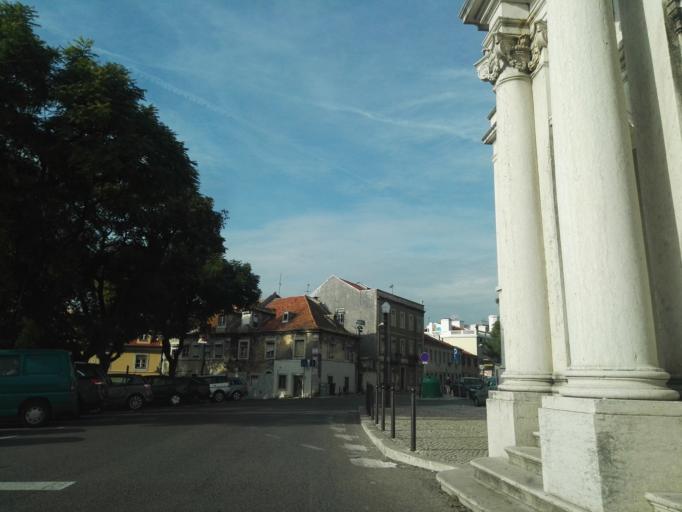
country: PT
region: Setubal
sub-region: Almada
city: Cacilhas
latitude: 38.7067
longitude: -9.1712
